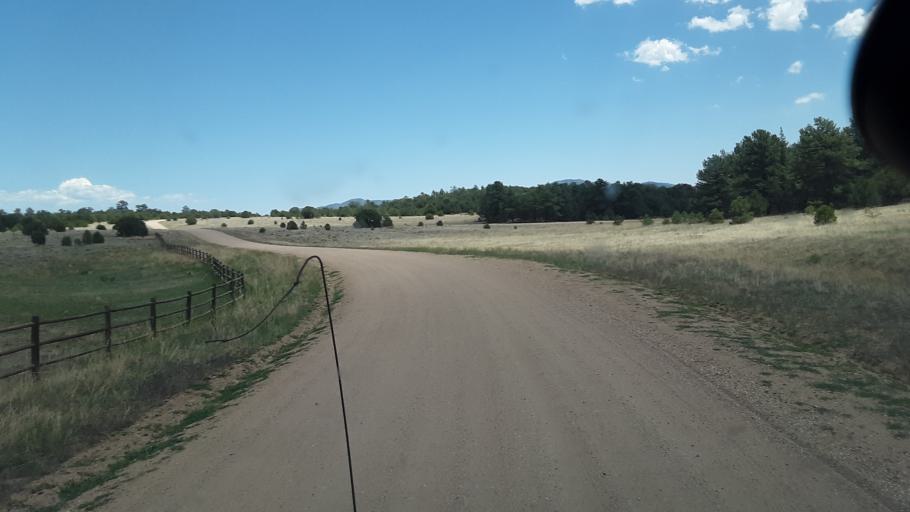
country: US
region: Colorado
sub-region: Custer County
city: Westcliffe
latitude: 38.2920
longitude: -105.4798
